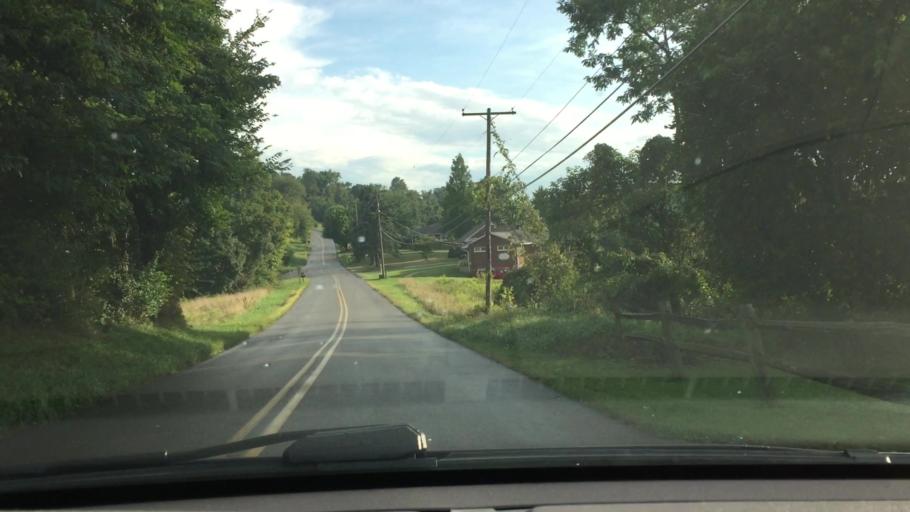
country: US
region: Pennsylvania
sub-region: Washington County
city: McGovern
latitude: 40.2113
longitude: -80.1854
